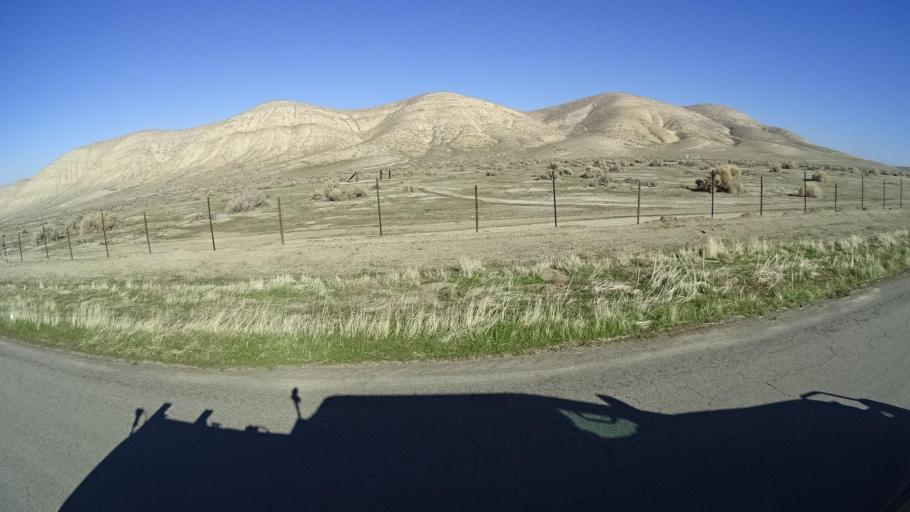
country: US
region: California
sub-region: Kern County
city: Maricopa
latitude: 34.9983
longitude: -119.3996
